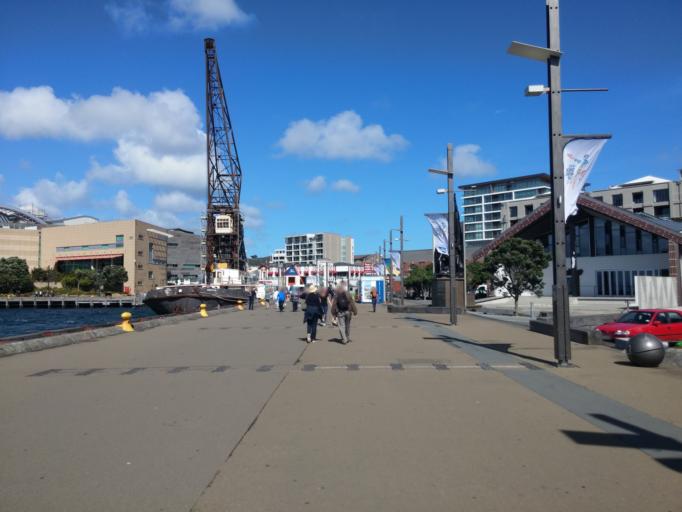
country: NZ
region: Wellington
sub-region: Wellington City
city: Wellington
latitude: -41.2885
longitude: 174.7801
